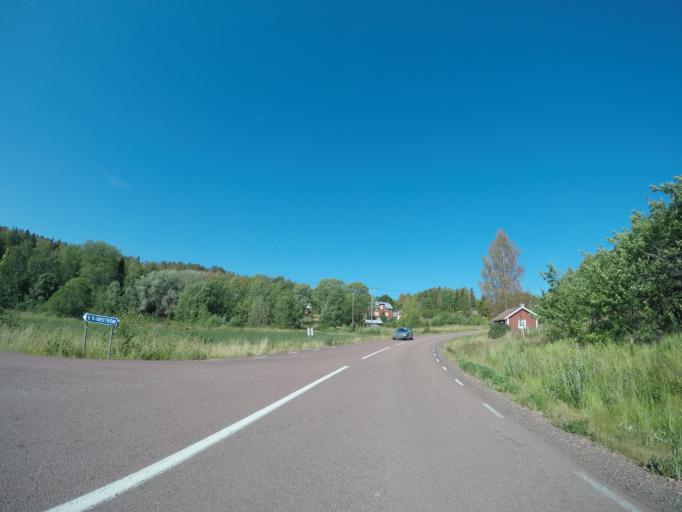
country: AX
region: Alands landsbygd
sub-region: Finstroem
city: Finstroem
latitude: 60.2722
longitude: 19.9229
